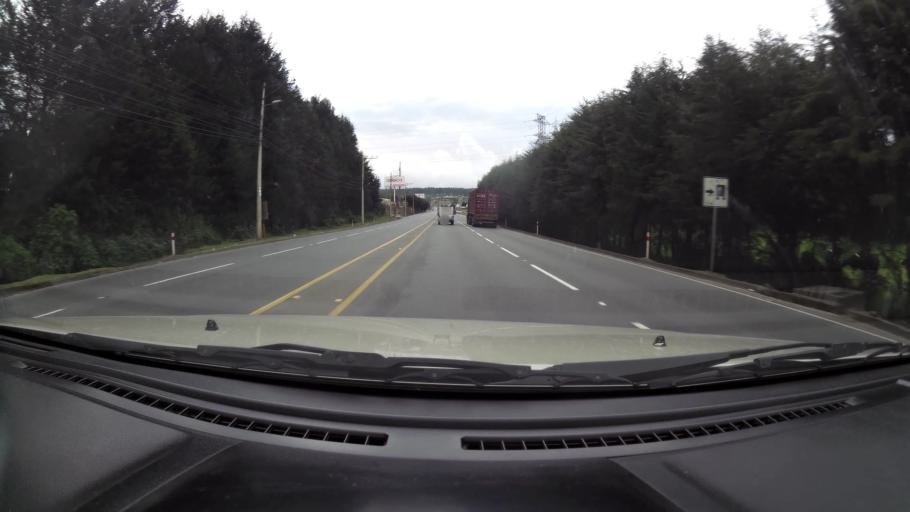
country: EC
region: Pichincha
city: Machachi
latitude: -0.4390
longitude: -78.6138
